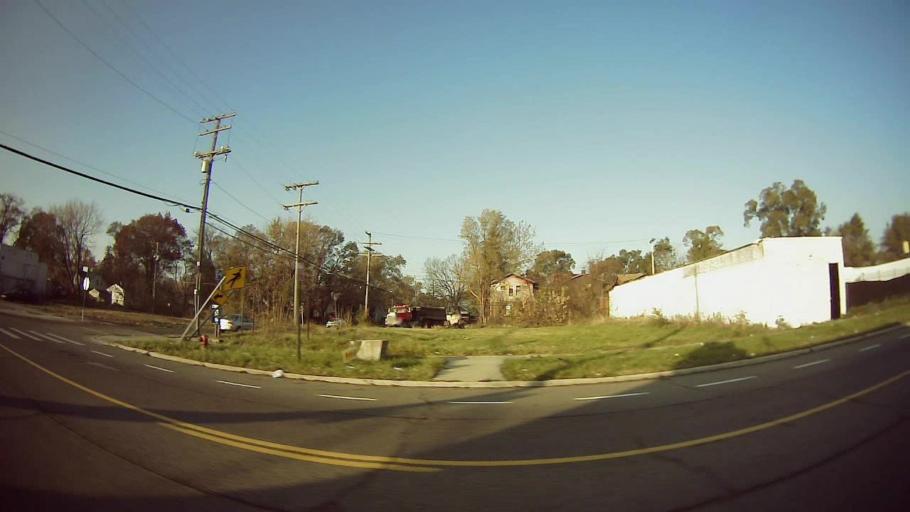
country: US
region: Michigan
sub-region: Wayne County
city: Highland Park
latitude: 42.3981
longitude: -83.1594
